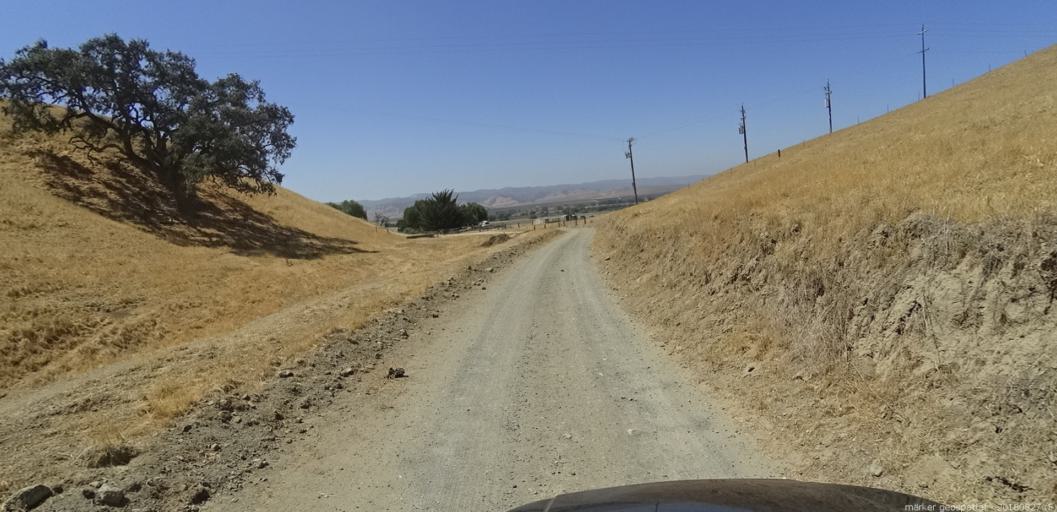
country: US
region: California
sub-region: Monterey County
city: King City
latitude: 36.0493
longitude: -120.9112
